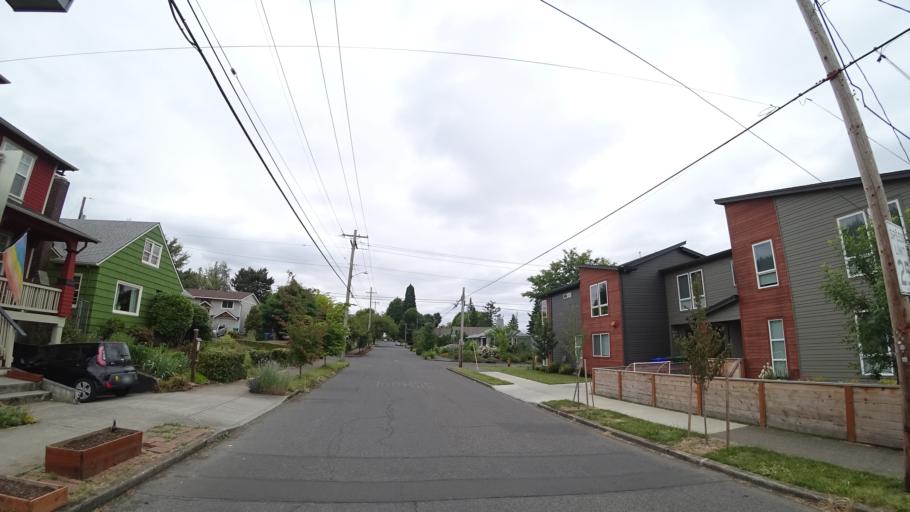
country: US
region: Oregon
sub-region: Multnomah County
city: Lents
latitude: 45.5112
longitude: -122.5853
